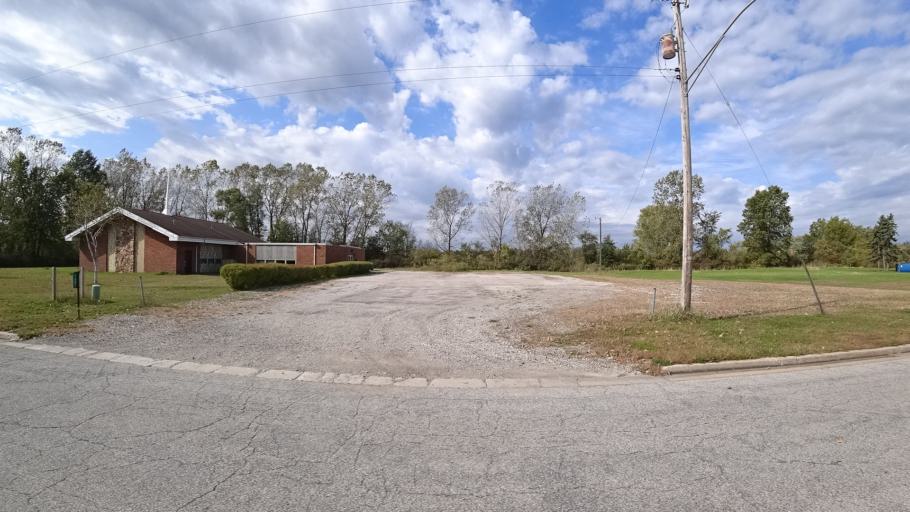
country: US
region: Indiana
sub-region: LaPorte County
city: Michigan City
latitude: 41.6676
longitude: -86.9006
